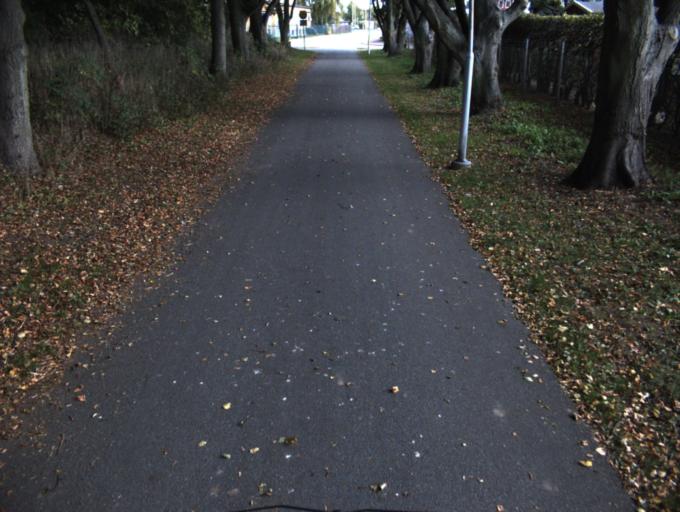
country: SE
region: Skane
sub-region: Helsingborg
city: Helsingborg
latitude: 56.0628
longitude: 12.7059
